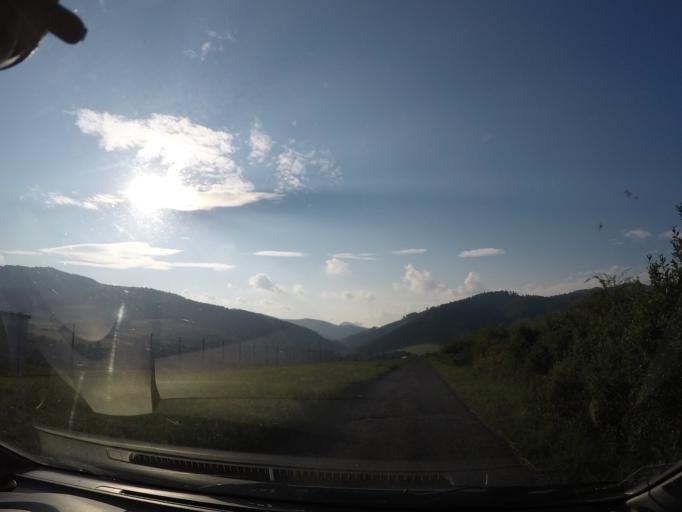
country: SK
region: Nitriansky
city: Bojnice
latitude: 48.8994
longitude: 18.6196
